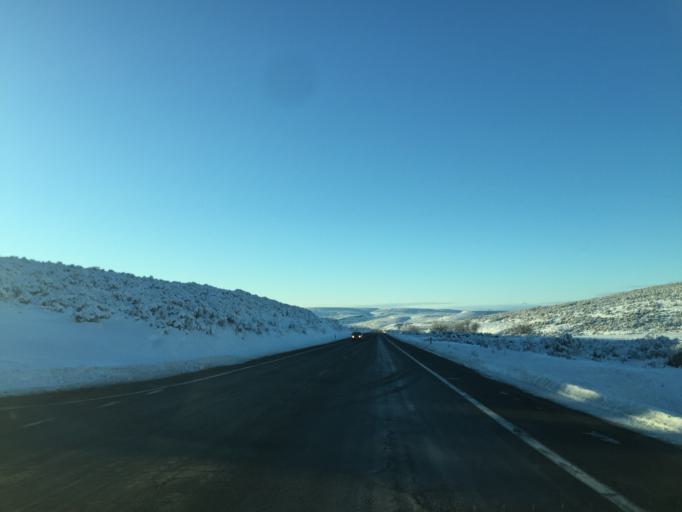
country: US
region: Washington
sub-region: Grant County
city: Soap Lake
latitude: 47.6016
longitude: -119.6192
